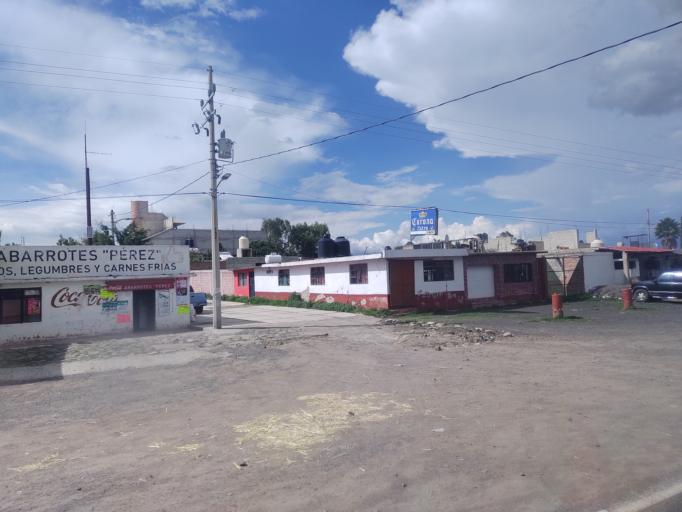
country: MX
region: Mexico
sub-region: Aculco
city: El Colorado
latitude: 20.0963
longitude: -99.7613
